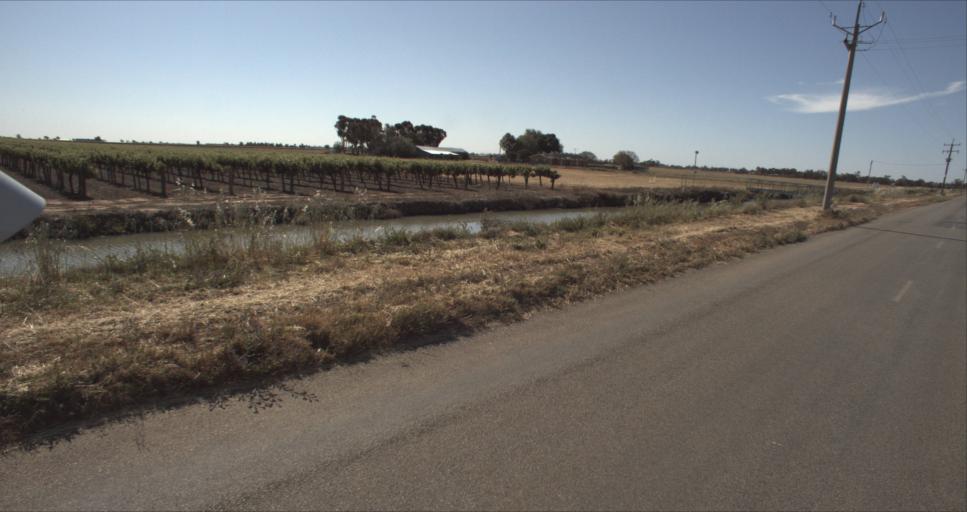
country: AU
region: New South Wales
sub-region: Leeton
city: Leeton
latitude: -34.5787
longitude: 146.3803
